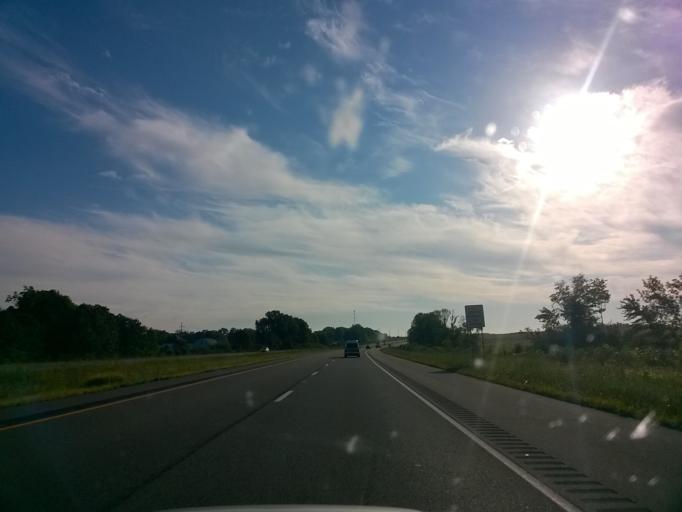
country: US
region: Indiana
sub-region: Warrick County
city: Boonville
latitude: 38.1990
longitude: -87.2767
